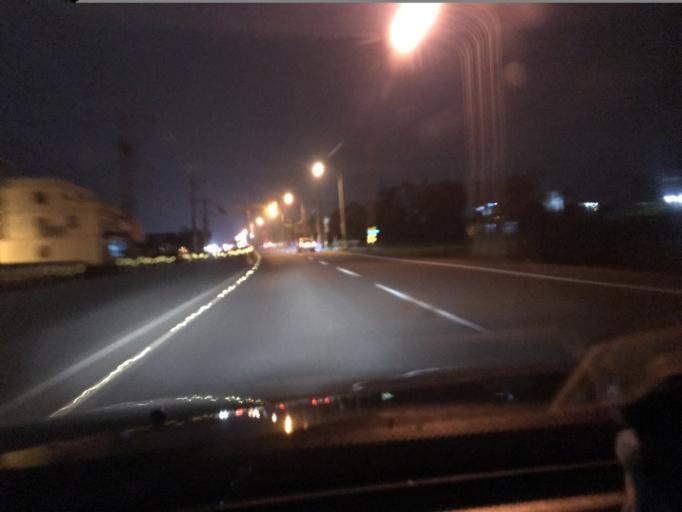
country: TW
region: Taiwan
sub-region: Hsinchu
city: Zhubei
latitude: 24.7786
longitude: 121.0708
